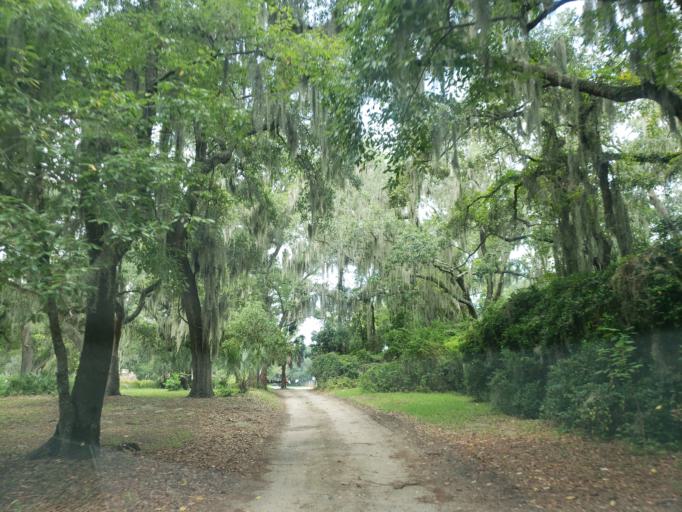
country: US
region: Georgia
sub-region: Chatham County
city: Wilmington Island
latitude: 31.9780
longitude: -80.9951
